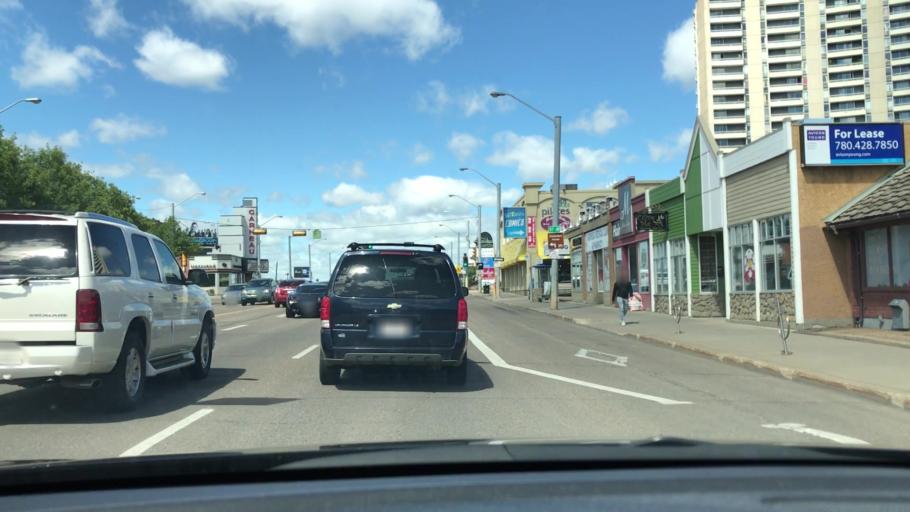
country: CA
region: Alberta
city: Edmonton
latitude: 53.5221
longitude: -113.5120
